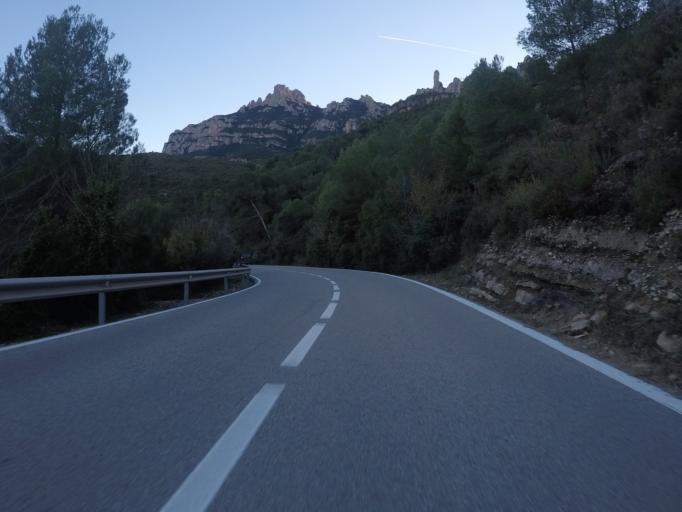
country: ES
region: Catalonia
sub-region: Provincia de Barcelona
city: Monistrol de Montserrat
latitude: 41.6151
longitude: 1.8314
